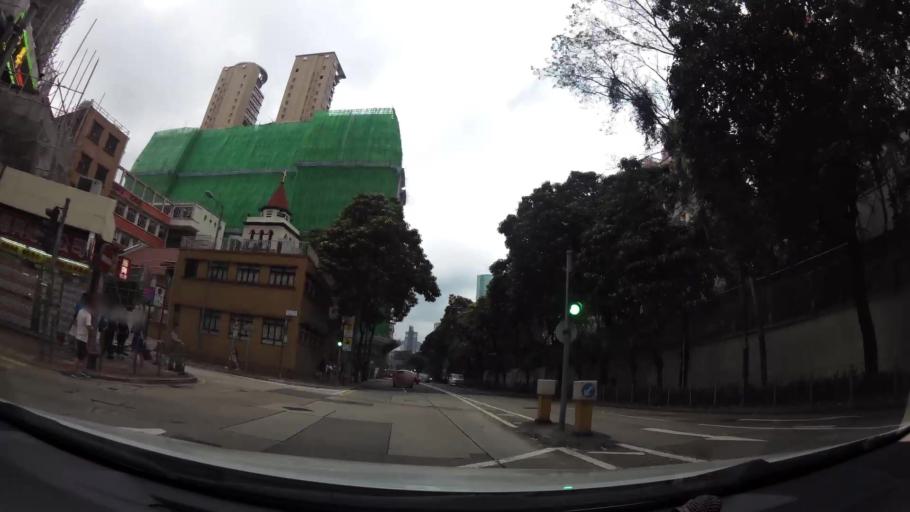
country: HK
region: Kowloon City
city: Kowloon
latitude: 22.3172
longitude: 114.1738
